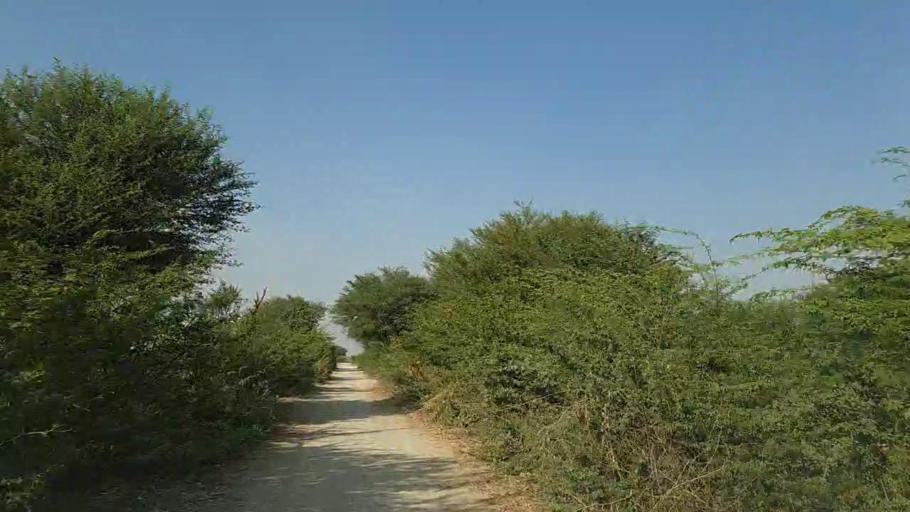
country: PK
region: Sindh
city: Naukot
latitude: 24.9291
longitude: 69.4879
